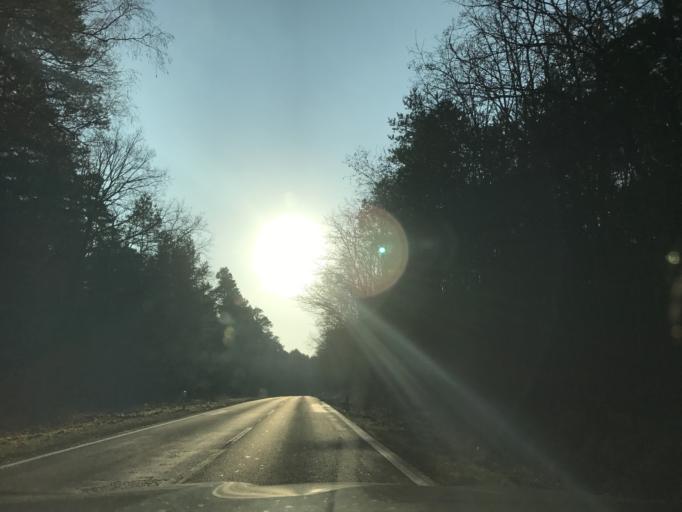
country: DE
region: Brandenburg
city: Wenzlow
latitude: 52.3392
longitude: 12.4974
